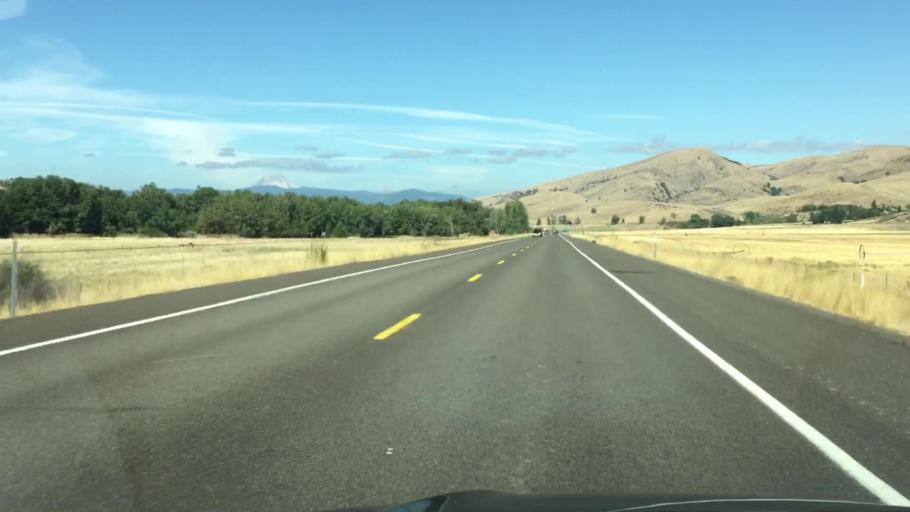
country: US
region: Oregon
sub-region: Wasco County
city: The Dalles
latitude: 45.2455
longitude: -121.1606
